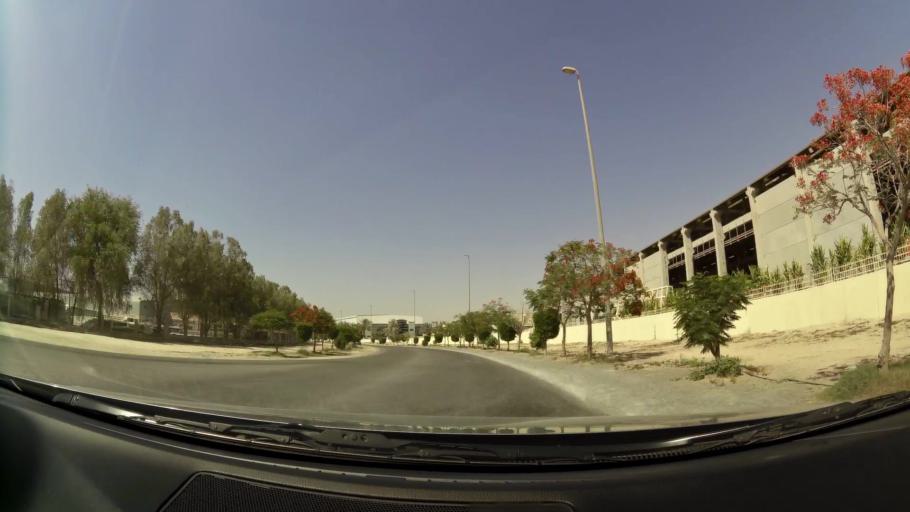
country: AE
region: Dubai
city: Dubai
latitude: 24.9709
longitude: 55.1757
